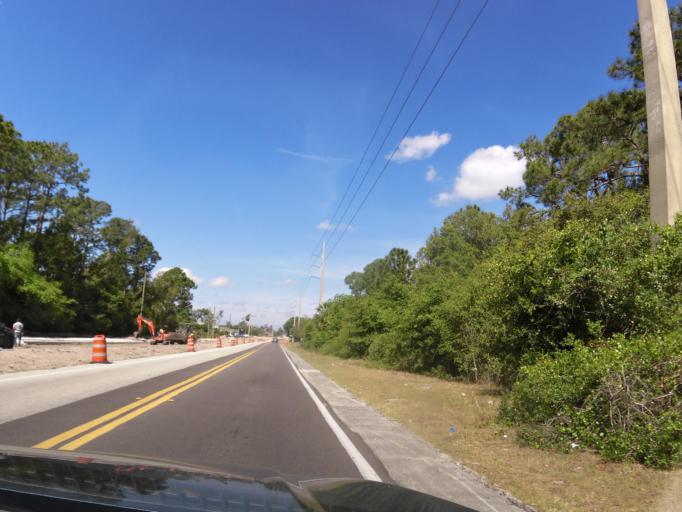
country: US
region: Florida
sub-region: Volusia County
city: Lake Helen
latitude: 28.9356
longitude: -81.2098
